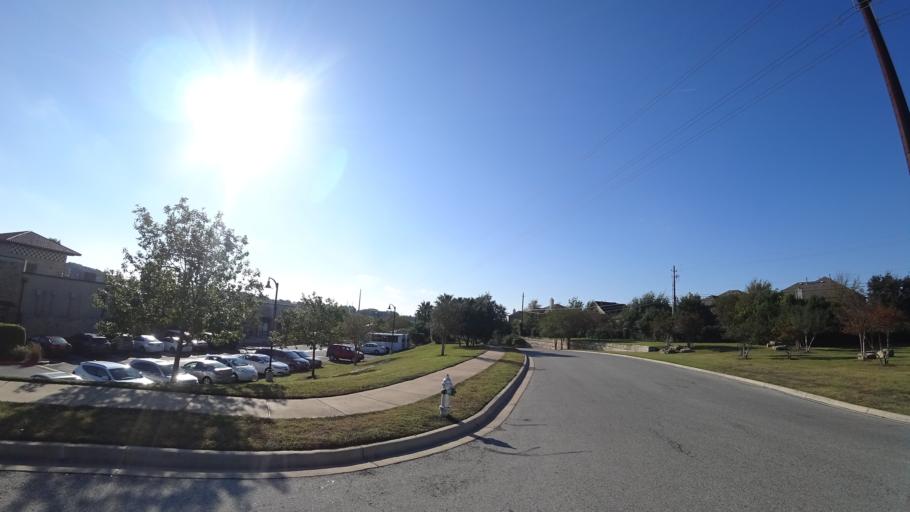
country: US
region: Texas
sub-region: Travis County
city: Hudson Bend
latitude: 30.3697
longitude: -97.8940
